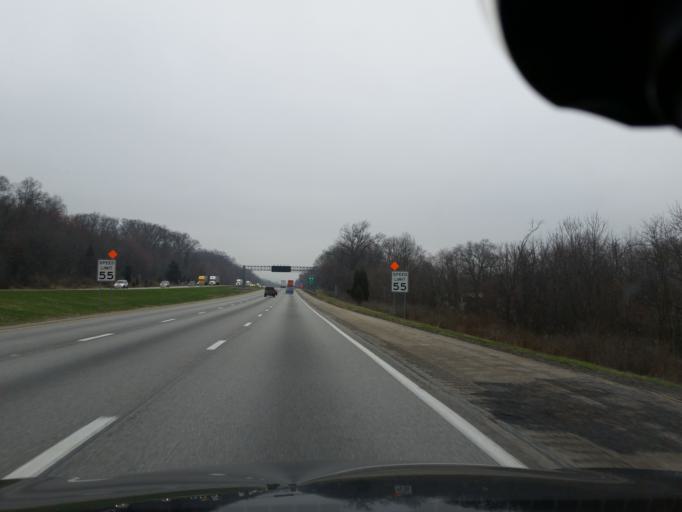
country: US
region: Pennsylvania
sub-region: Cumberland County
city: Enola
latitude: 40.3082
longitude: -76.9472
